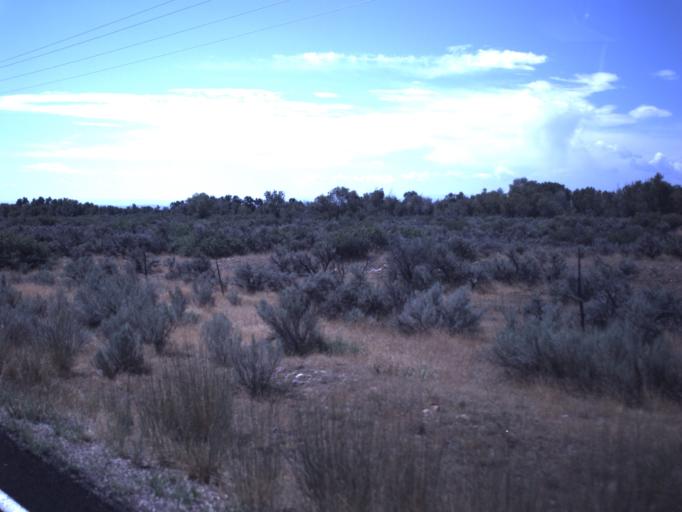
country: US
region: Utah
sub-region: Duchesne County
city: Roosevelt
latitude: 40.4173
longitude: -109.9198
